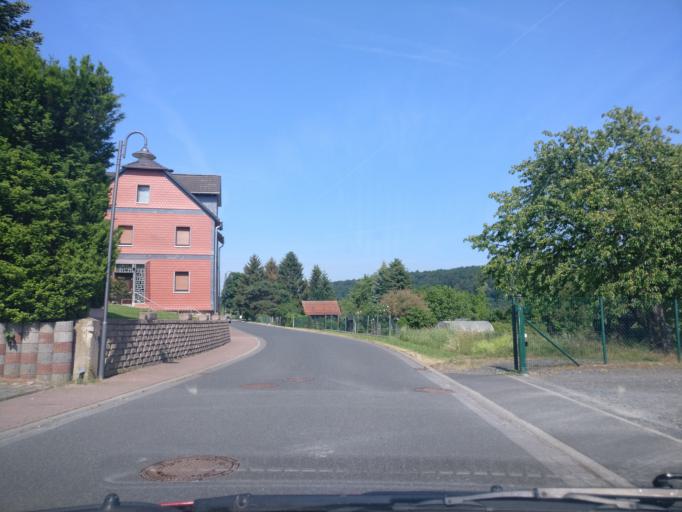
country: DE
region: Lower Saxony
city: Scheden
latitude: 51.3873
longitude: 9.7481
